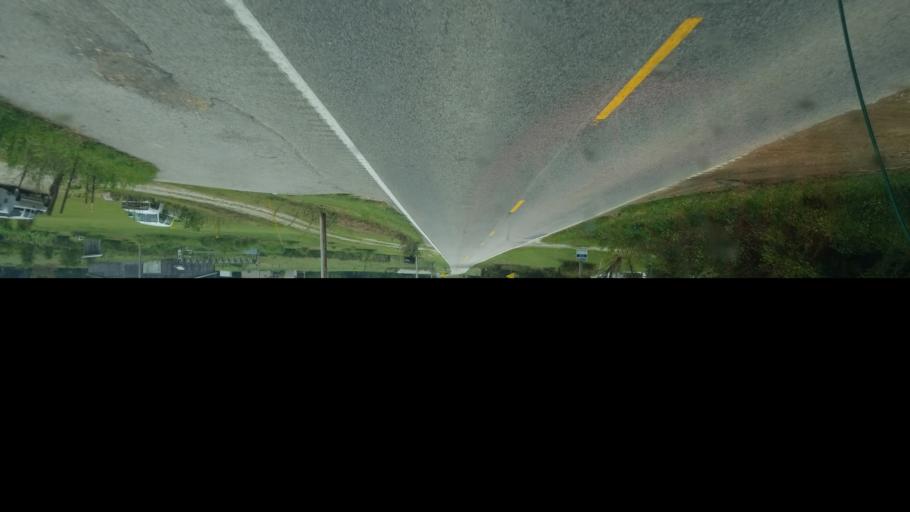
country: US
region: Kentucky
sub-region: Rowan County
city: Morehead
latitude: 38.2689
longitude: -83.4286
